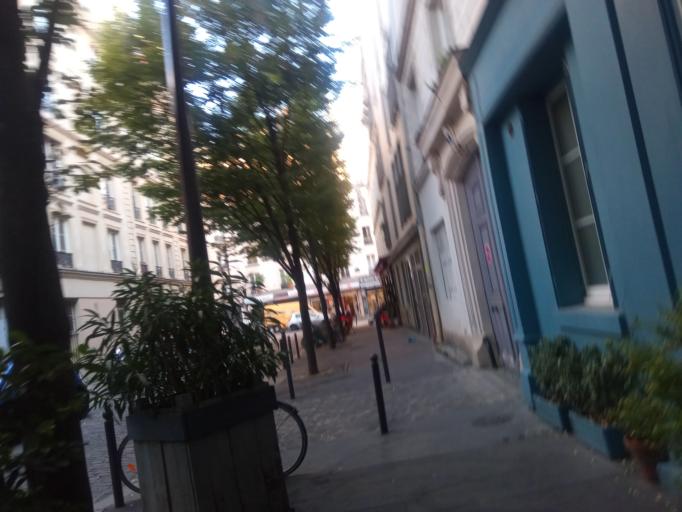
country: FR
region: Ile-de-France
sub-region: Departement de Seine-Saint-Denis
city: Le Pre-Saint-Gervais
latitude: 48.8624
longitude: 2.3832
